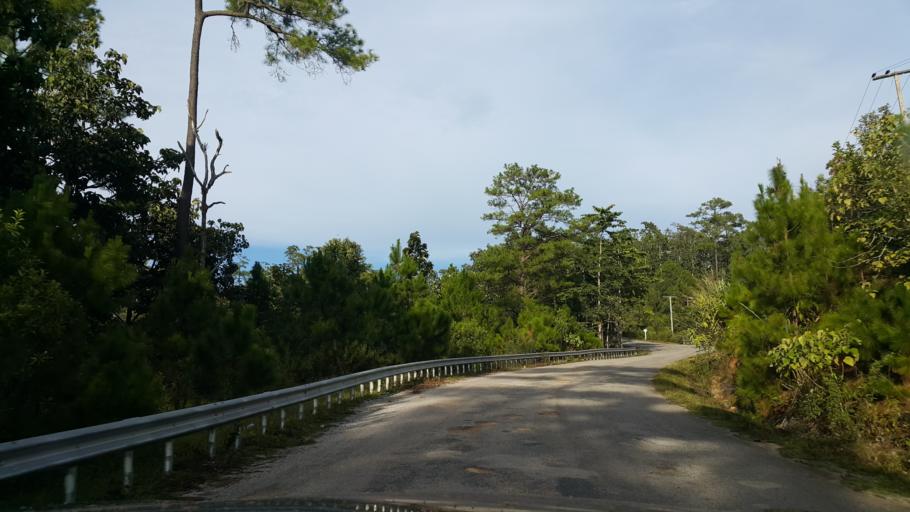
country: TH
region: Chiang Mai
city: Chaem Luang
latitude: 19.1012
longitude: 98.3502
